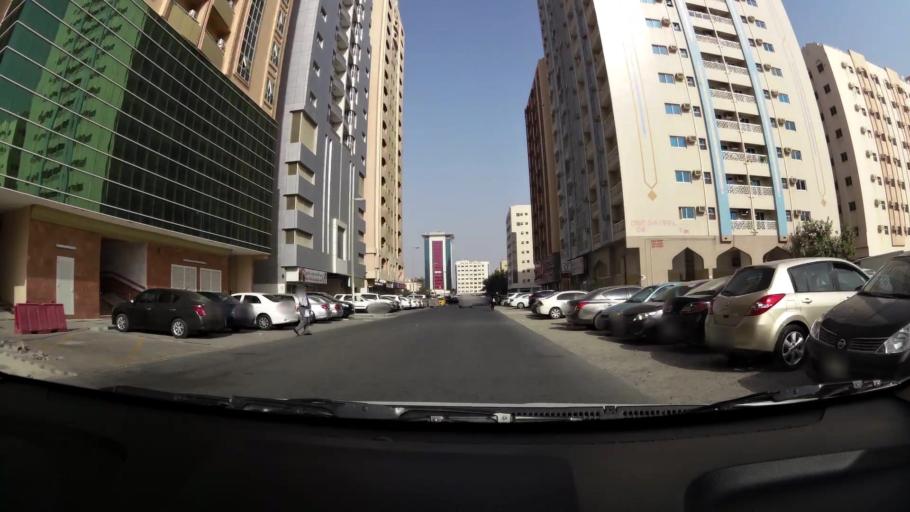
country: AE
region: Ash Shariqah
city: Sharjah
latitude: 25.3386
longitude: 55.3965
